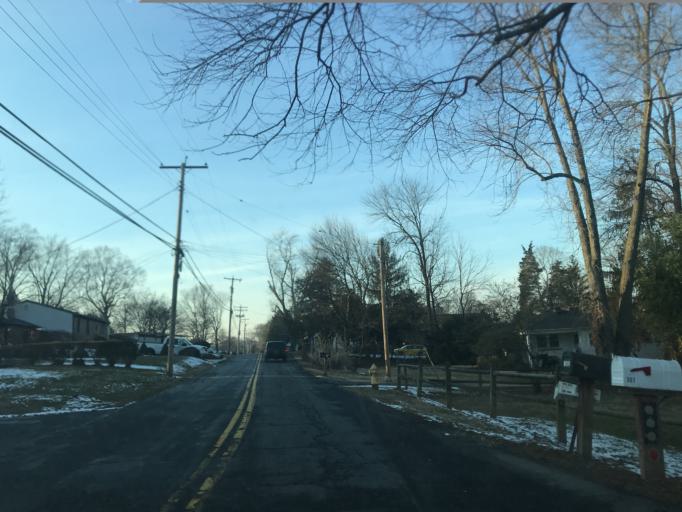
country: US
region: Maryland
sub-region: Harford County
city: Riverside
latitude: 39.4391
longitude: -76.2518
